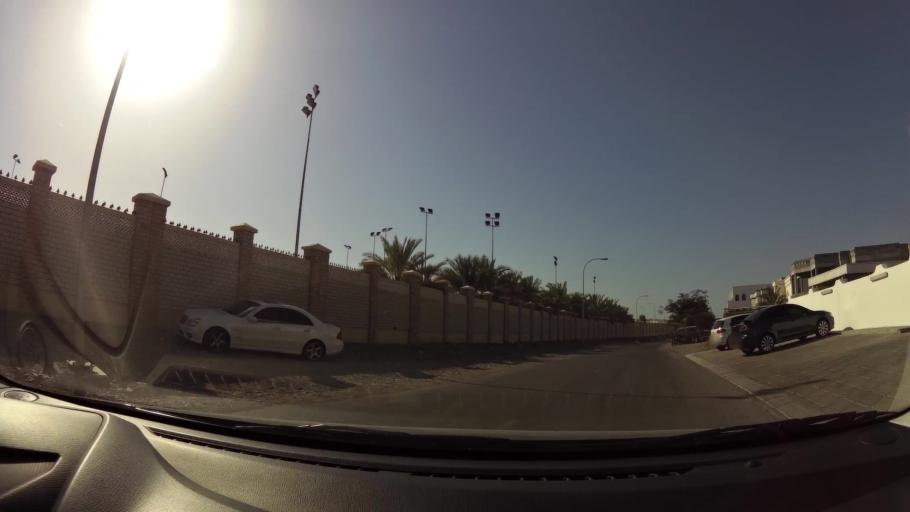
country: OM
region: Muhafazat Masqat
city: As Sib al Jadidah
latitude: 23.6192
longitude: 58.2003
